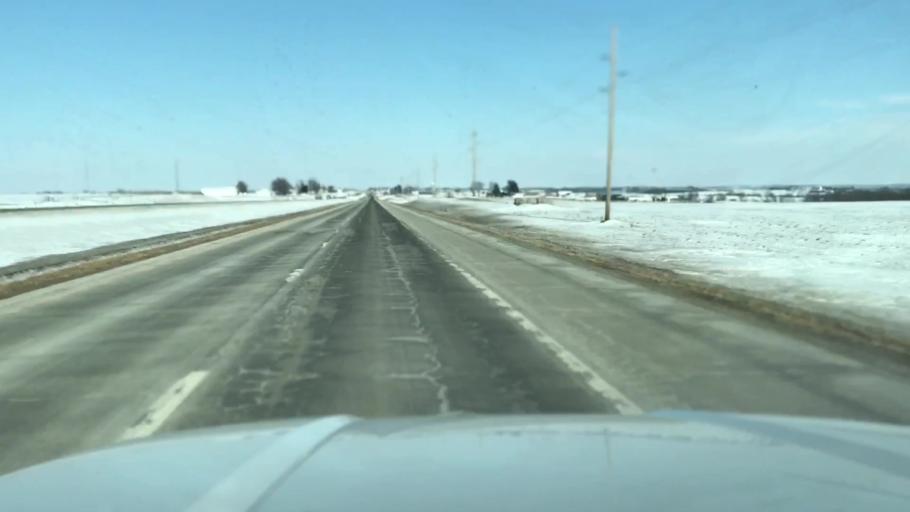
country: US
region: Missouri
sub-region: Nodaway County
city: Maryville
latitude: 40.2307
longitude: -94.8677
